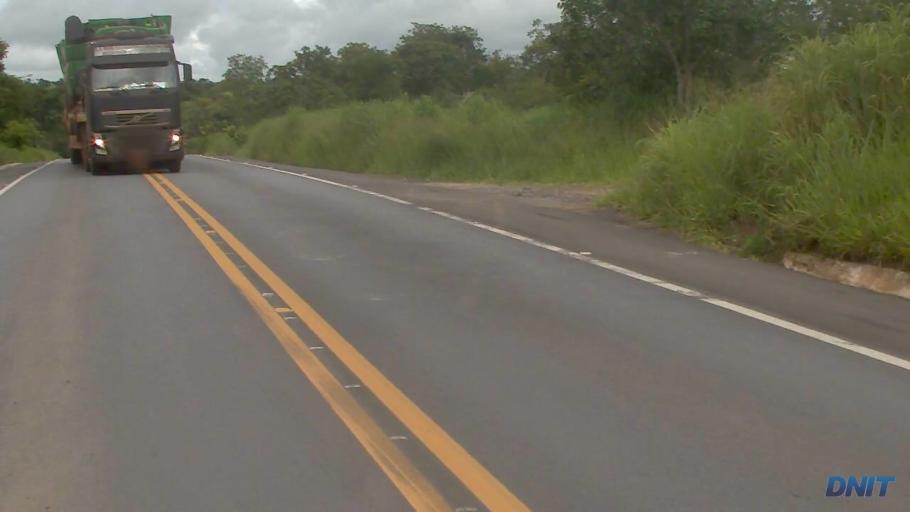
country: BR
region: Goias
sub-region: Posse
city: Posse
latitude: -14.2902
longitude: -46.4290
